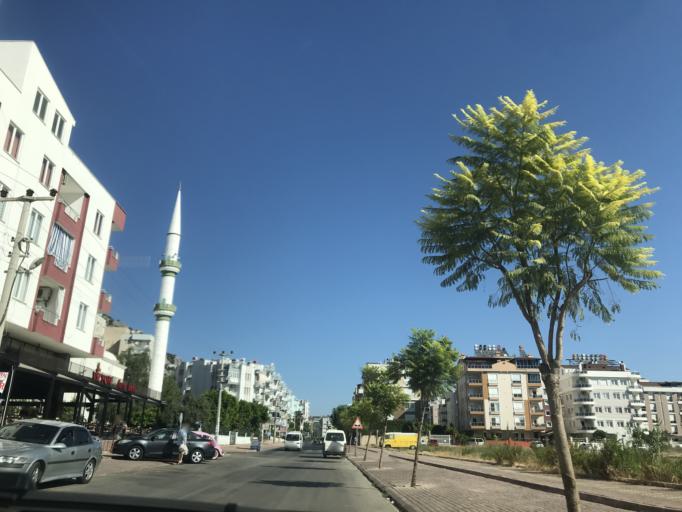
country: TR
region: Antalya
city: Cakirlar
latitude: 36.8537
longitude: 30.6026
